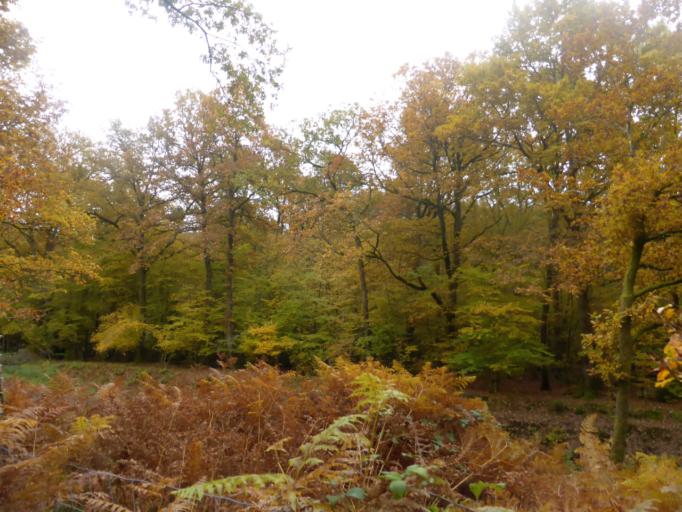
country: BE
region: Wallonia
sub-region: Province du Luxembourg
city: Herbeumont
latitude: 49.7306
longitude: 5.2011
